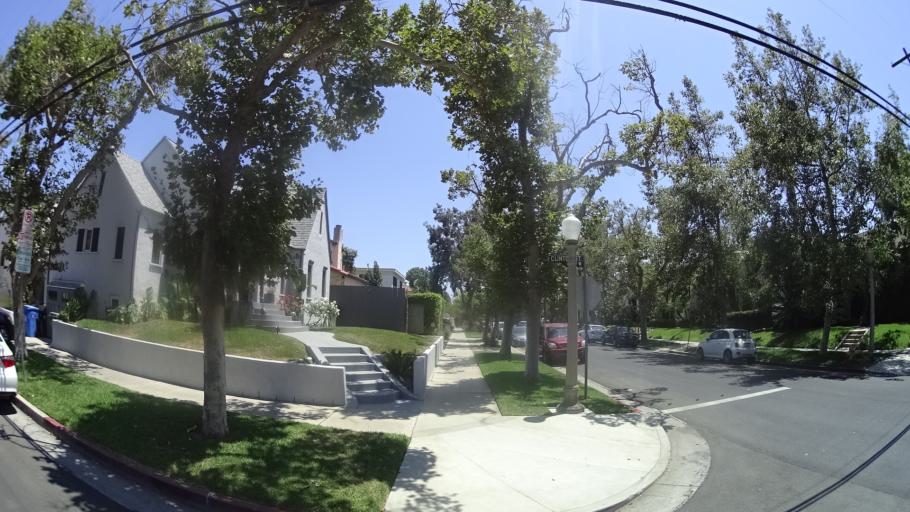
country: US
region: California
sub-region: Los Angeles County
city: West Hollywood
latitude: 34.0819
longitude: -118.3416
